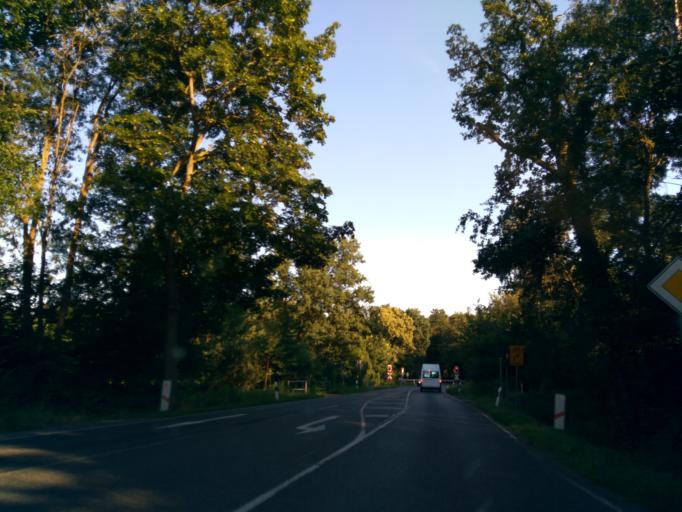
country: DE
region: Brandenburg
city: Brieselang
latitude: 52.5951
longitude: 13.0492
